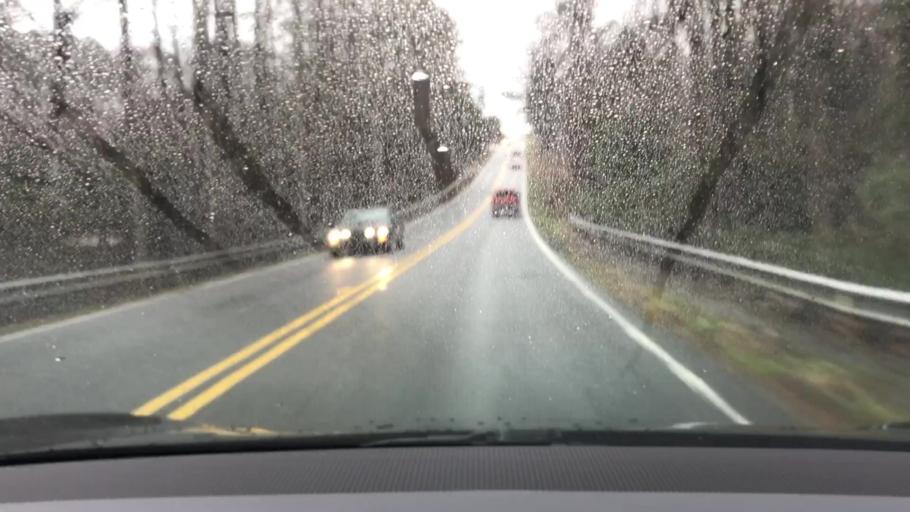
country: US
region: Georgia
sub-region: Forsyth County
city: Cumming
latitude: 34.1866
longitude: -84.1150
